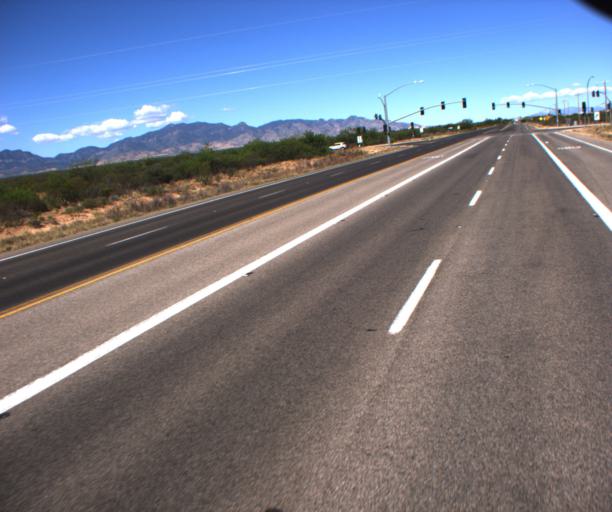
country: US
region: Arizona
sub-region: Cochise County
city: Sierra Vista Southeast
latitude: 31.5516
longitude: -110.1884
